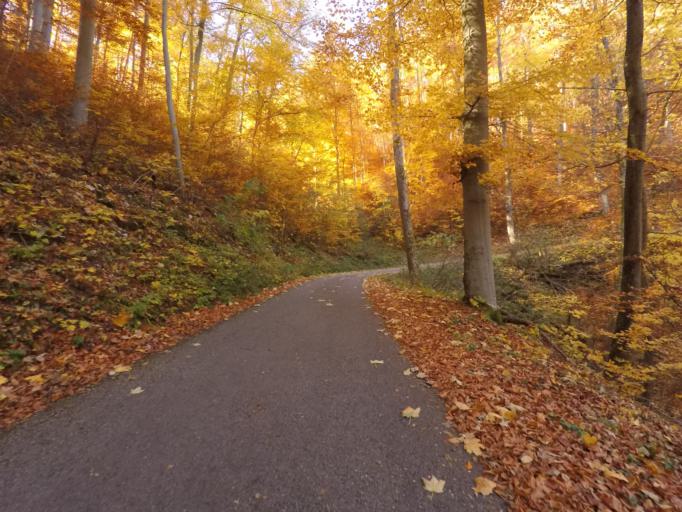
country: DE
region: Baden-Wuerttemberg
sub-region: Tuebingen Region
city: Pfullingen
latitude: 48.4388
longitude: 9.2328
